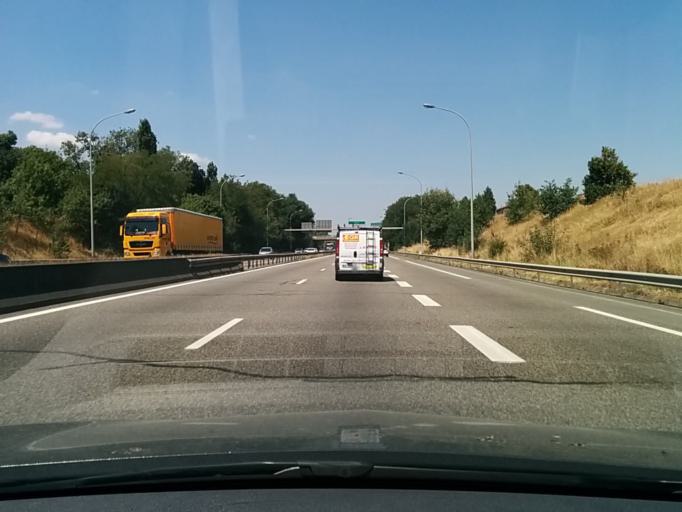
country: FR
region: Midi-Pyrenees
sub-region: Departement de la Haute-Garonne
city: Blagnac
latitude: 43.6068
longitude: 1.3917
